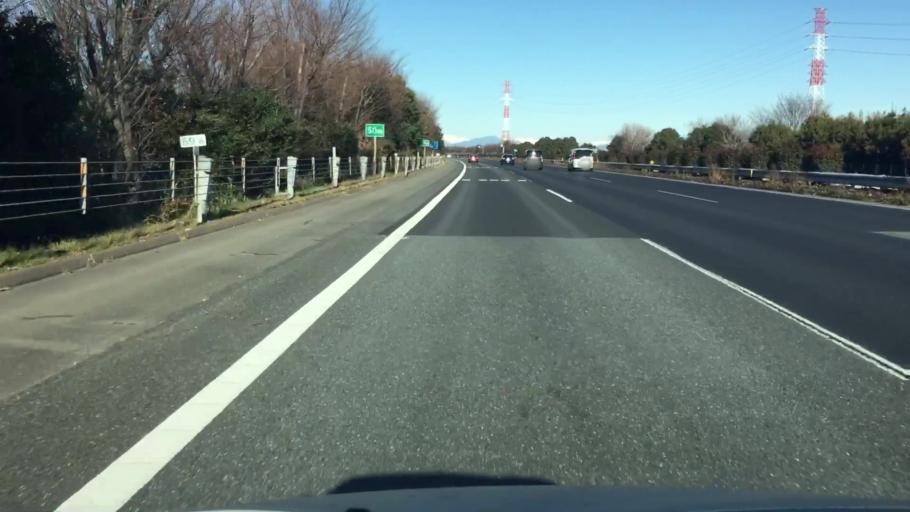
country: JP
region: Saitama
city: Yorii
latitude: 36.1470
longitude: 139.2220
